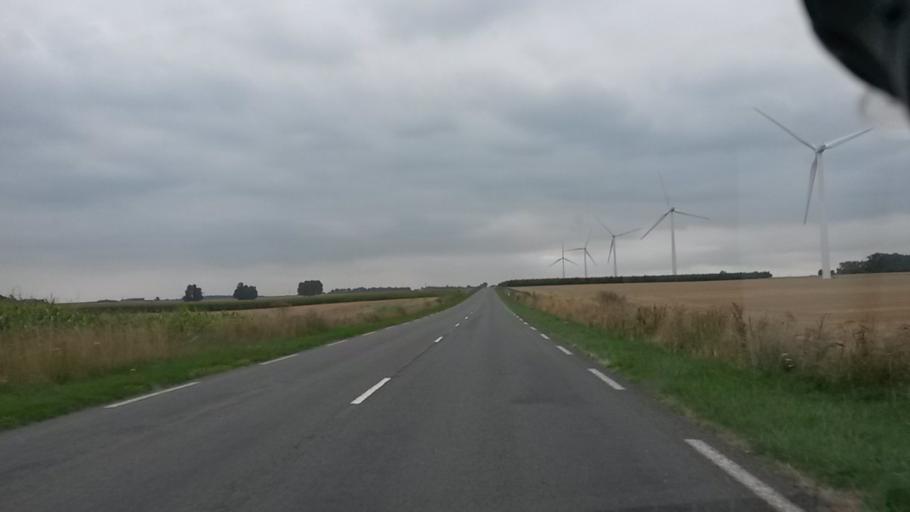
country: FR
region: Haute-Normandie
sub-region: Departement de la Seine-Maritime
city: Aumale
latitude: 49.7718
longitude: 1.8397
